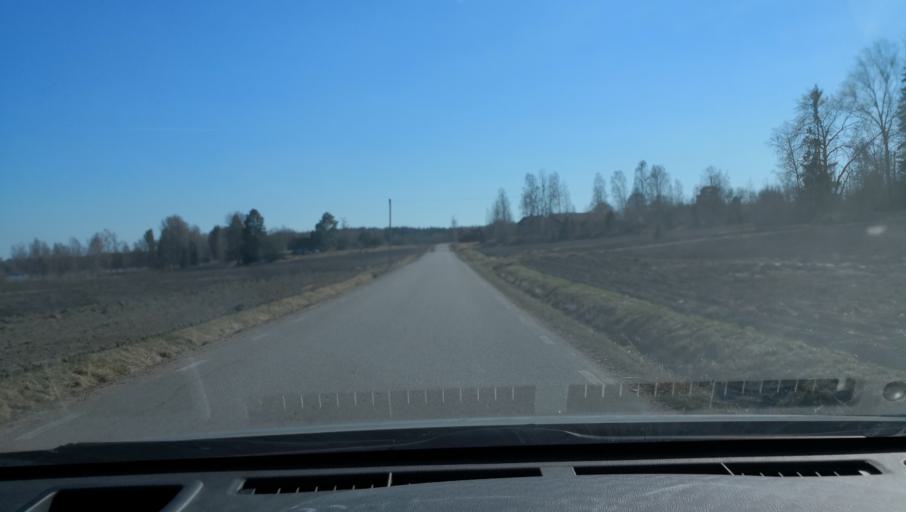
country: SE
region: Vaestmanland
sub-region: Sala Kommun
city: Sala
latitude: 60.0811
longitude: 16.4967
